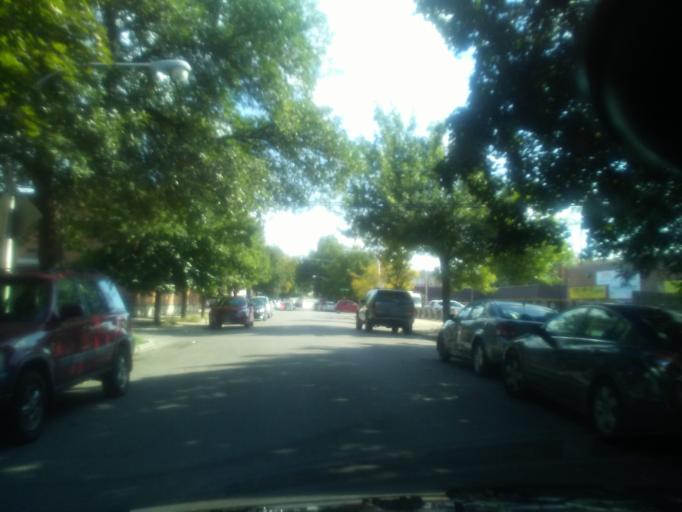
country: US
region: Illinois
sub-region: Cook County
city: Lincolnwood
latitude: 41.9688
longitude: -87.7318
